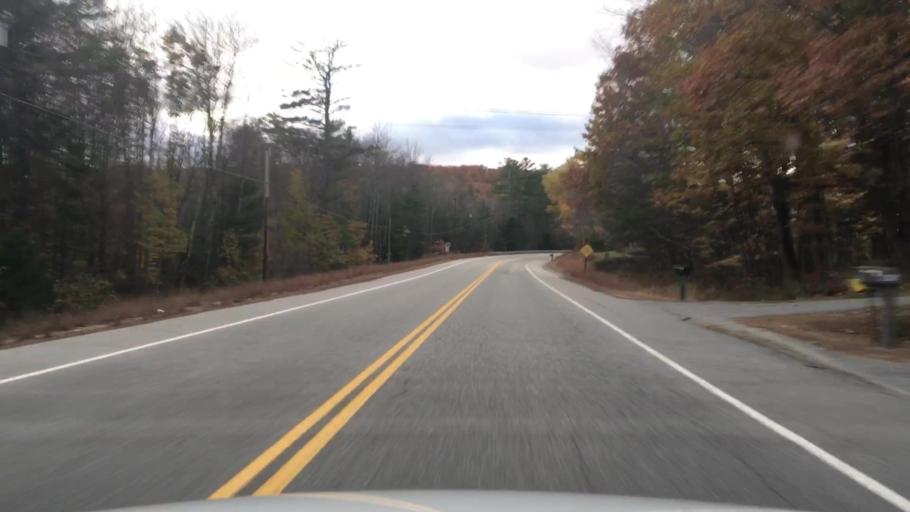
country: US
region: Maine
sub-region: Androscoggin County
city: Livermore
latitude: 44.4042
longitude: -70.2702
